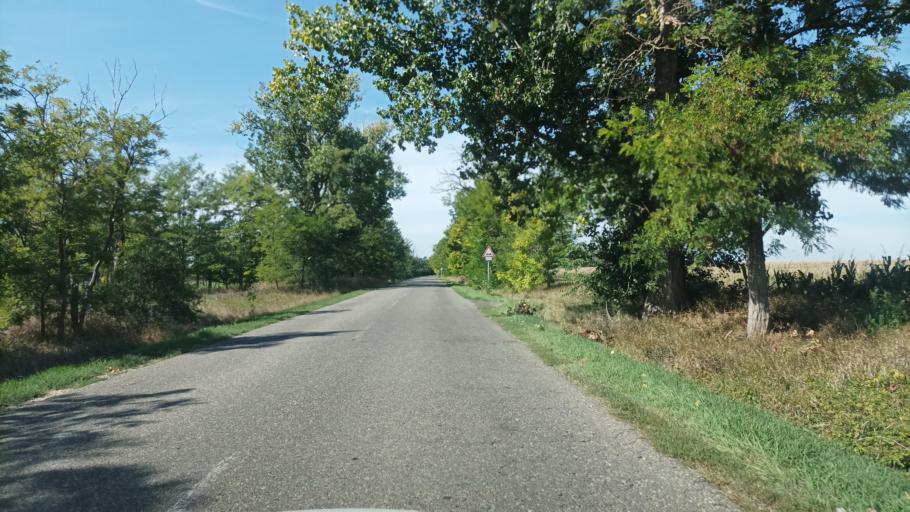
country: HU
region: Pest
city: Zsambok
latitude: 47.5516
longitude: 19.5901
